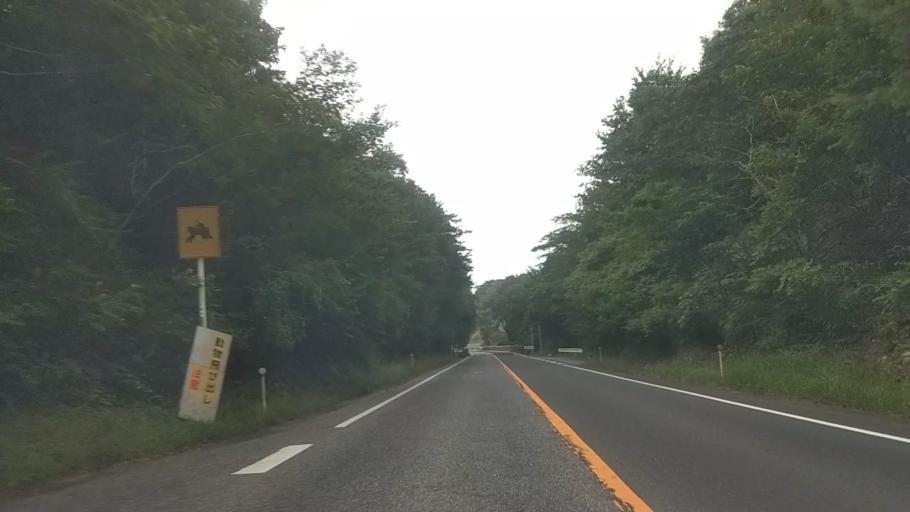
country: JP
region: Chiba
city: Kawaguchi
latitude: 35.2199
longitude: 140.0382
